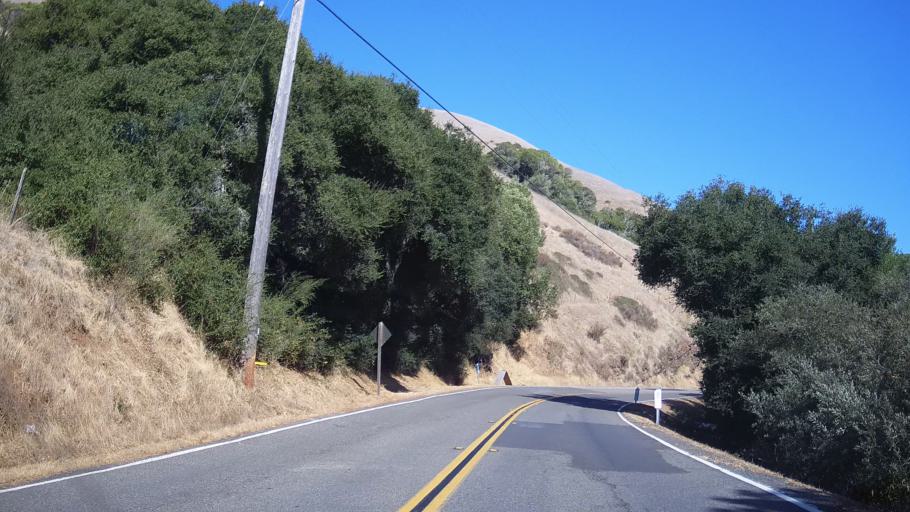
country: US
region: California
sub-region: Marin County
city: Lagunitas-Forest Knolls
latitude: 38.0706
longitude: -122.7685
